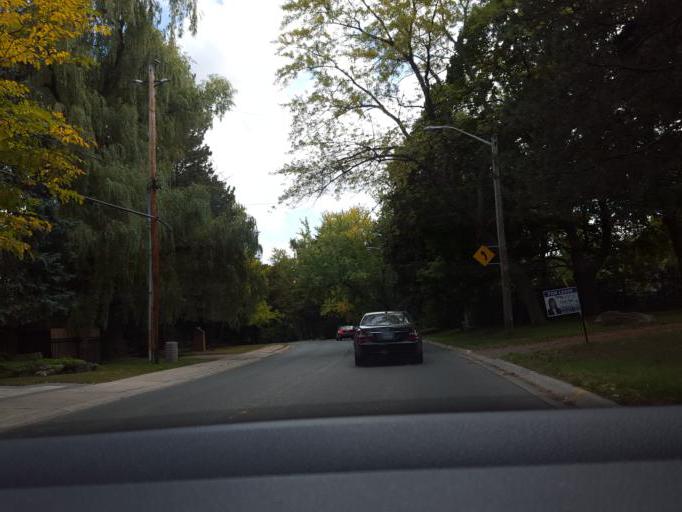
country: CA
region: Ontario
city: Willowdale
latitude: 43.7368
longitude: -79.3708
